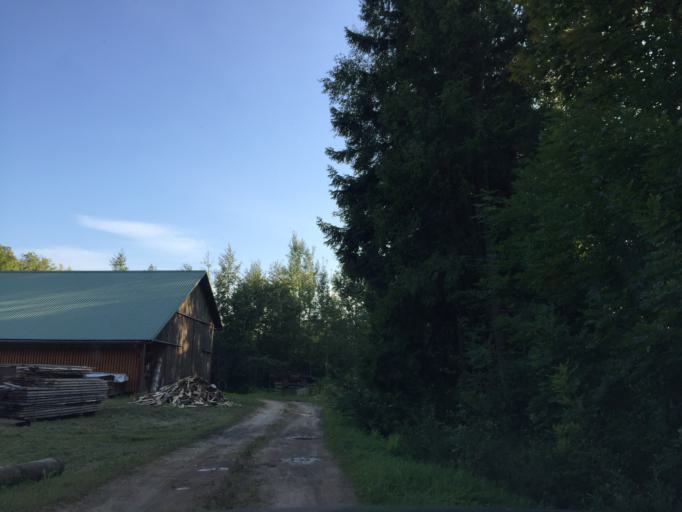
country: LV
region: Limbazu Rajons
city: Limbazi
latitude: 57.5613
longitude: 24.7858
